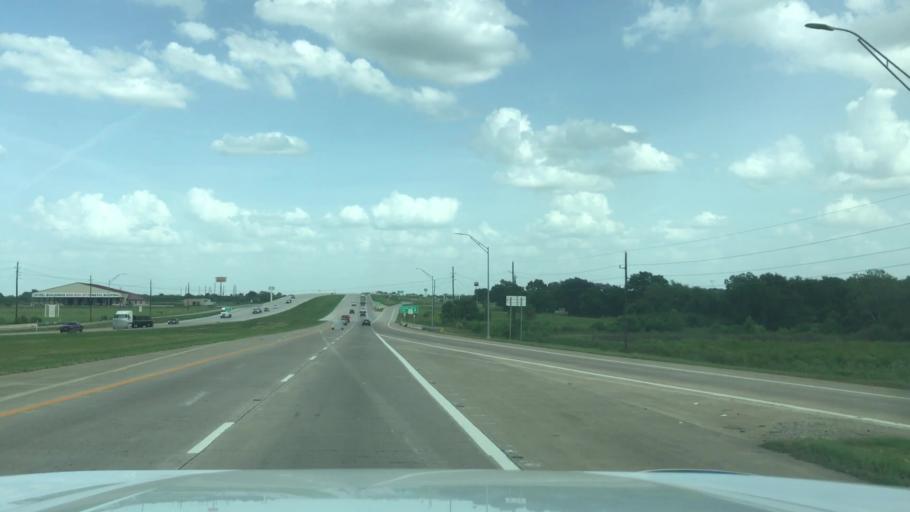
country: US
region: Texas
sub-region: Waller County
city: Waller
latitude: 30.0698
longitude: -95.9304
